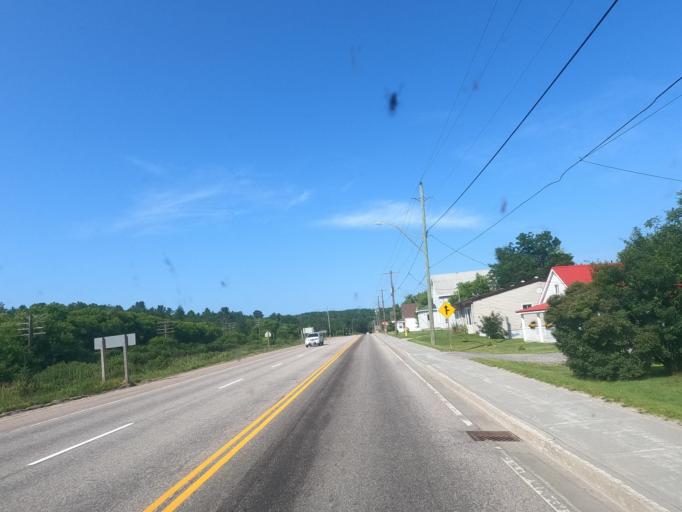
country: CA
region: Ontario
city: Mattawa
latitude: 46.3087
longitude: -78.7151
